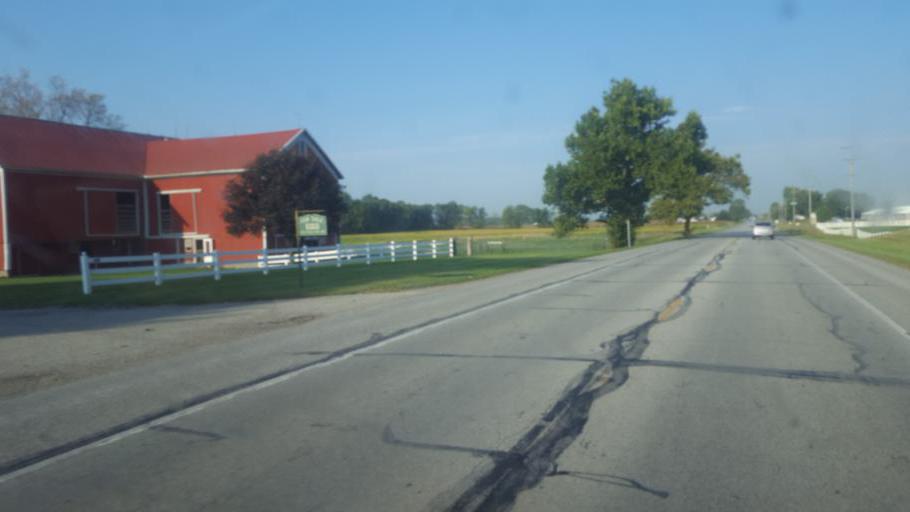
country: US
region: Indiana
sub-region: LaGrange County
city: Lagrange
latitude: 41.6407
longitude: -85.5068
